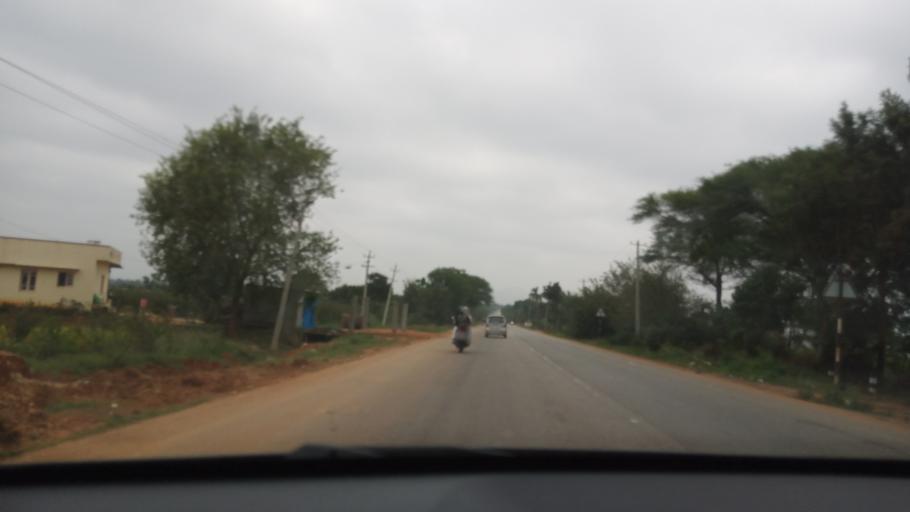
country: IN
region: Karnataka
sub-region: Chikkaballapur
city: Sidlaghatta
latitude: 13.2736
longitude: 77.9517
